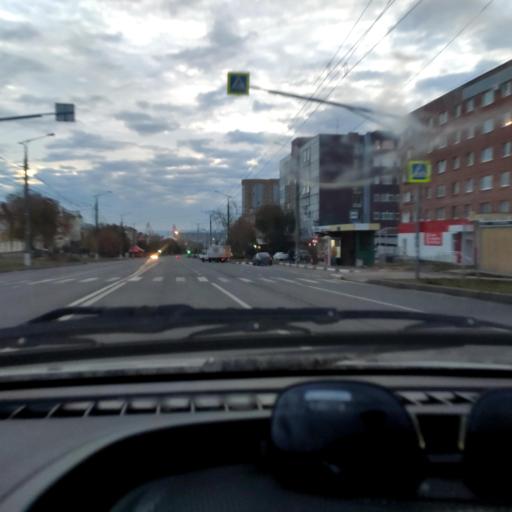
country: RU
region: Samara
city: Zhigulevsk
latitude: 53.4748
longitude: 49.4682
